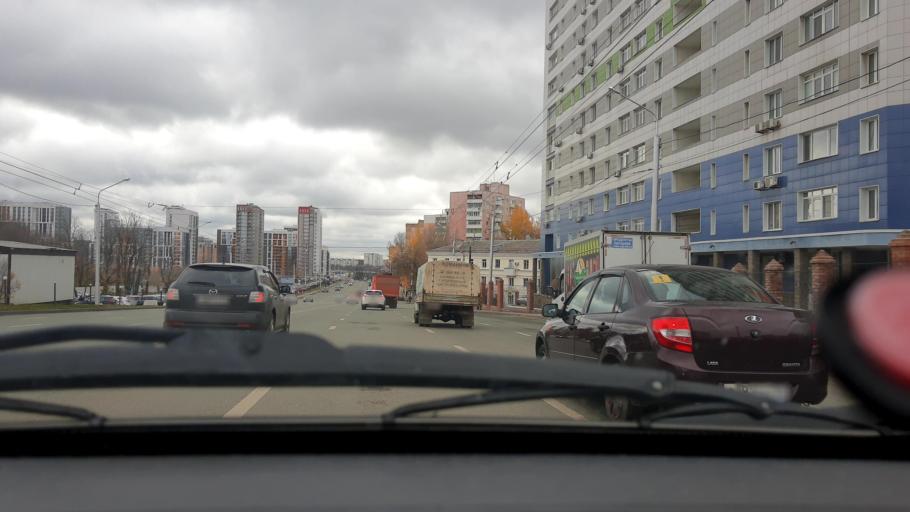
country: RU
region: Bashkortostan
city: Ufa
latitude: 54.7620
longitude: 56.0227
